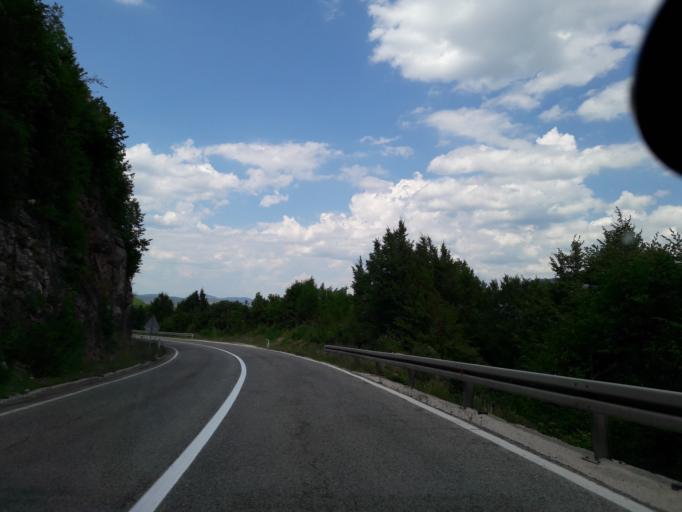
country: BA
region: Republika Srpska
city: Mrkonjic Grad
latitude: 44.4980
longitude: 17.1524
